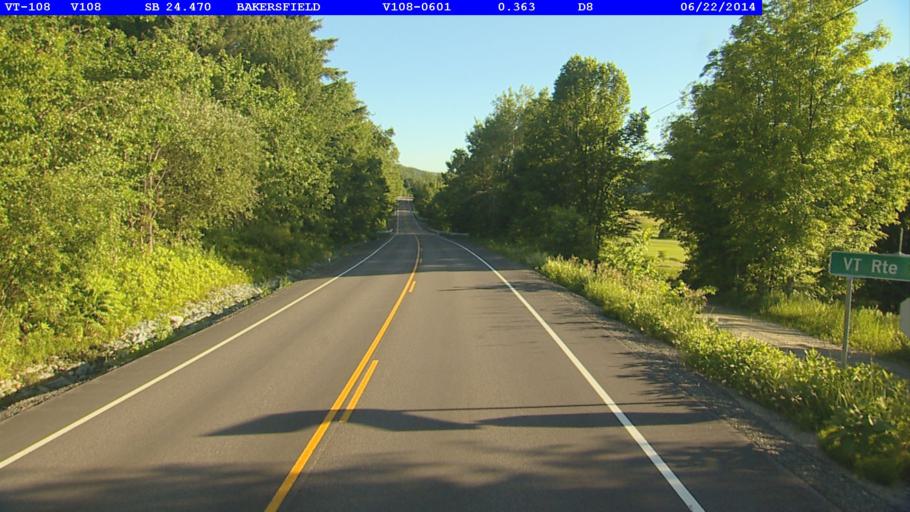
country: US
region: Vermont
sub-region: Franklin County
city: Enosburg Falls
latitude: 44.7387
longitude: -72.8255
